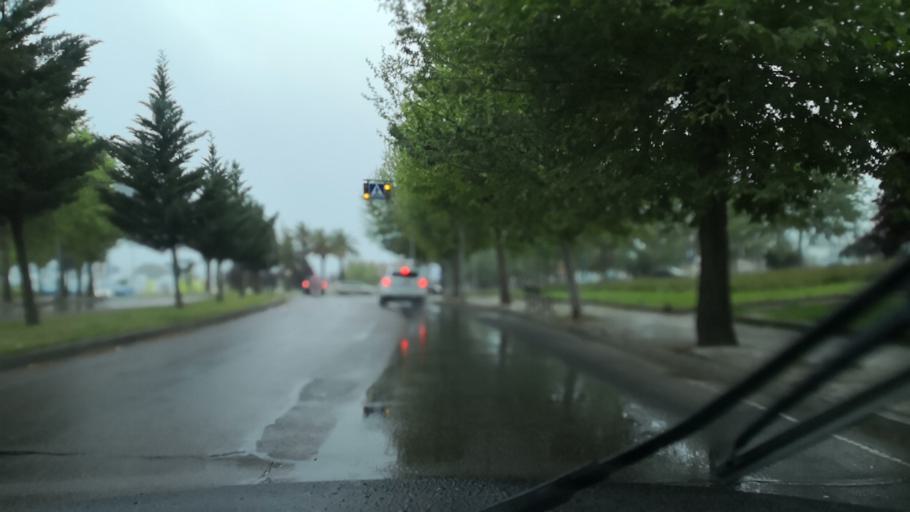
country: ES
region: Extremadura
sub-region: Provincia de Badajoz
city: Badajoz
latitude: 38.8628
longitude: -6.9726
